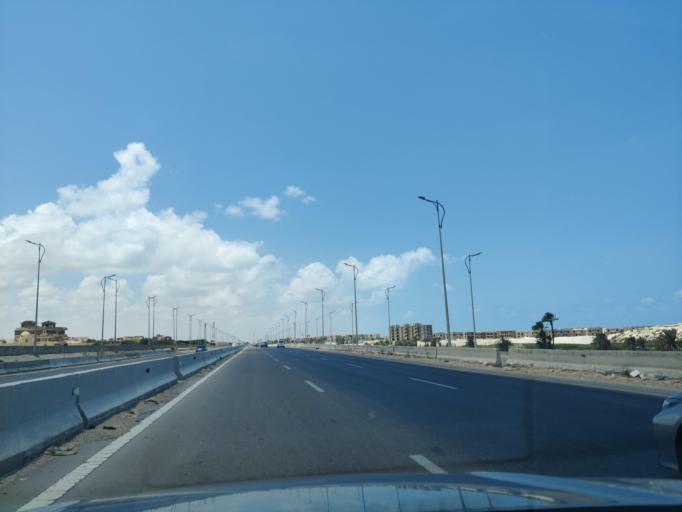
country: EG
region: Muhafazat Matruh
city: Al `Alamayn
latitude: 30.9167
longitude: 29.4486
